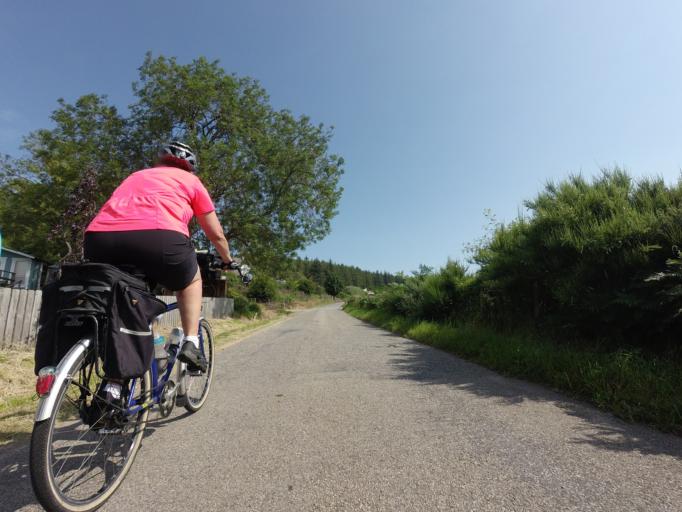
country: GB
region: Scotland
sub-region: Highland
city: Invergordon
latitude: 57.7572
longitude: -4.1332
